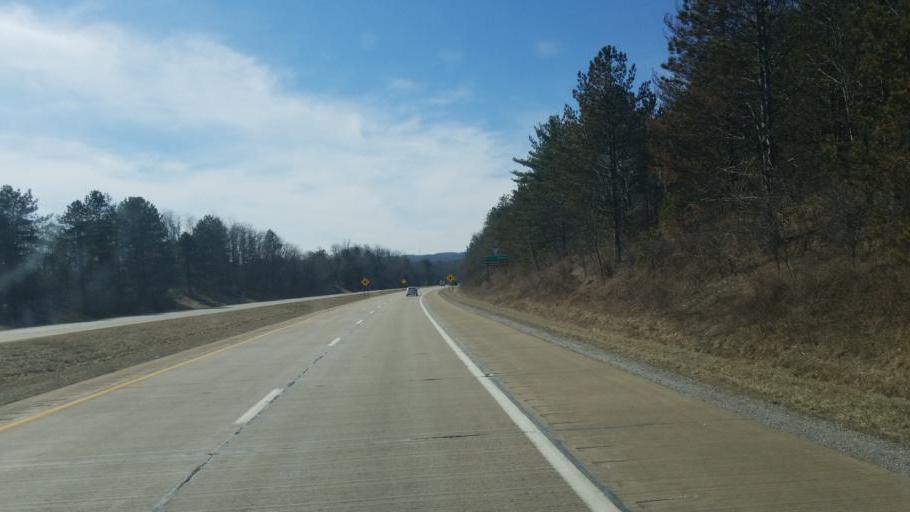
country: US
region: Ohio
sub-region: Ashland County
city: Ashland
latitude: 40.7808
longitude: -82.3702
